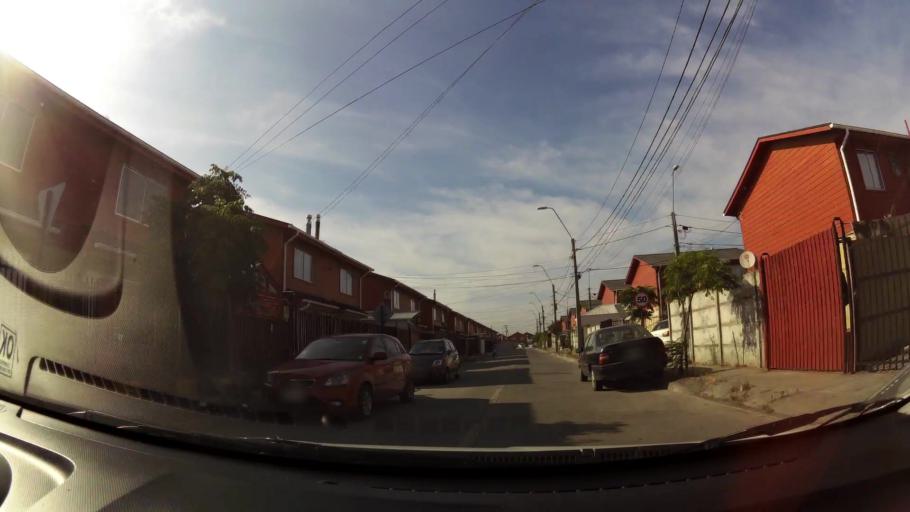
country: CL
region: Biobio
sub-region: Provincia de Concepcion
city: Talcahuano
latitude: -36.7951
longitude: -73.1151
